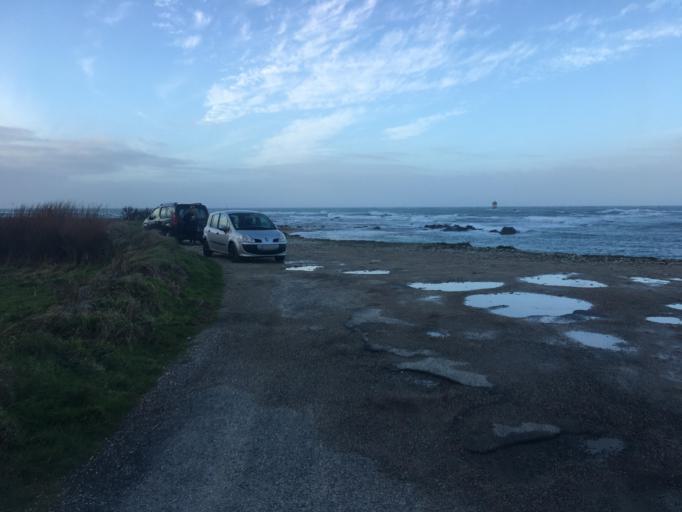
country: FR
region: Lower Normandy
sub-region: Departement de la Manche
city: Beaumont-Hague
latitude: 49.7261
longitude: -1.9242
